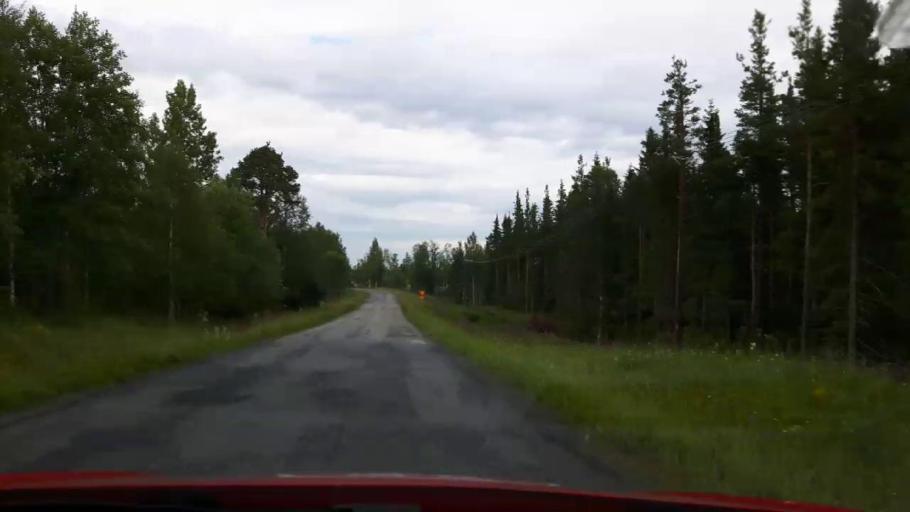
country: SE
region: Jaemtland
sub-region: Stroemsunds Kommun
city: Stroemsund
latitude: 63.5354
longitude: 15.3544
